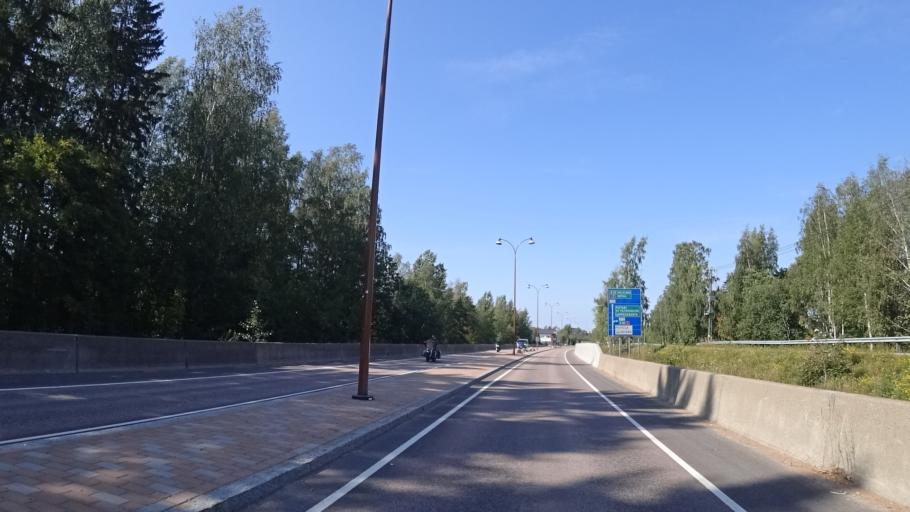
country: FI
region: Kymenlaakso
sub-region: Kotka-Hamina
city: Hamina
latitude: 60.5640
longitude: 27.1705
